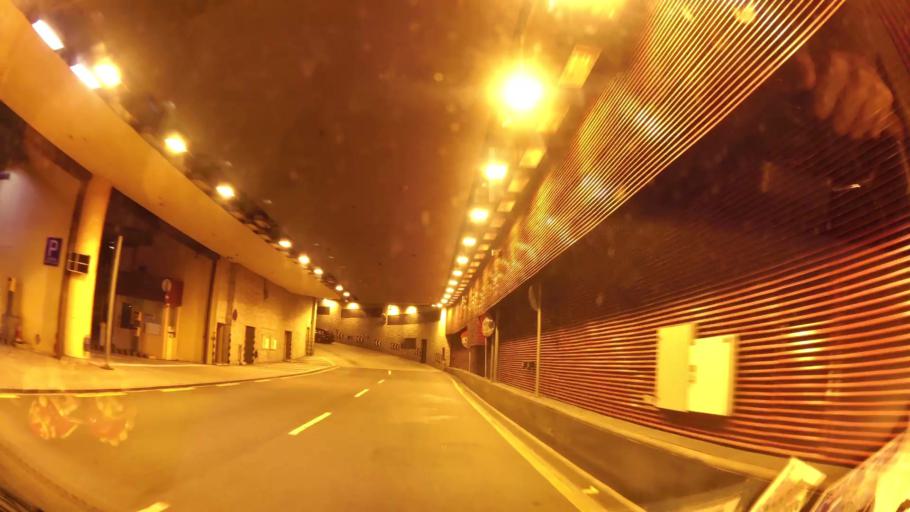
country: MO
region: Macau
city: Macau
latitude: 22.1977
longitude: 113.5472
